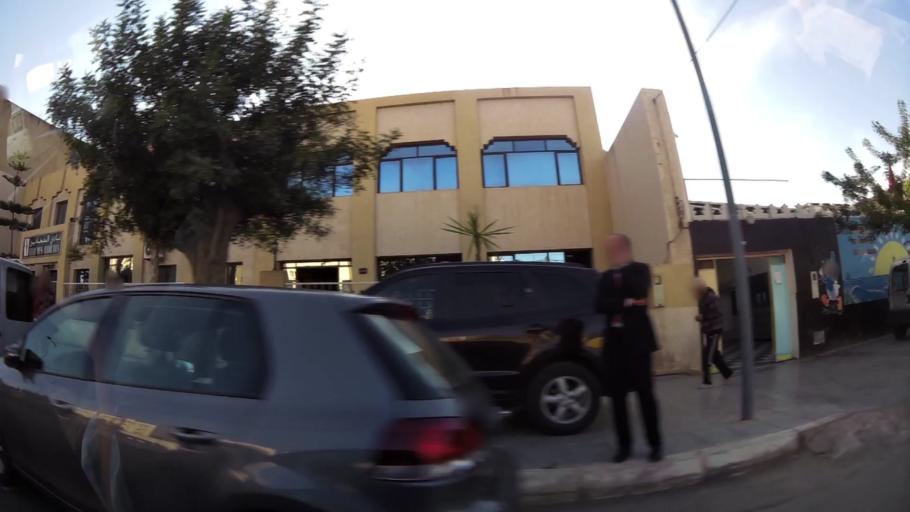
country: MA
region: Oriental
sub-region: Oujda-Angad
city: Oujda
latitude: 34.6935
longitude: -1.9121
